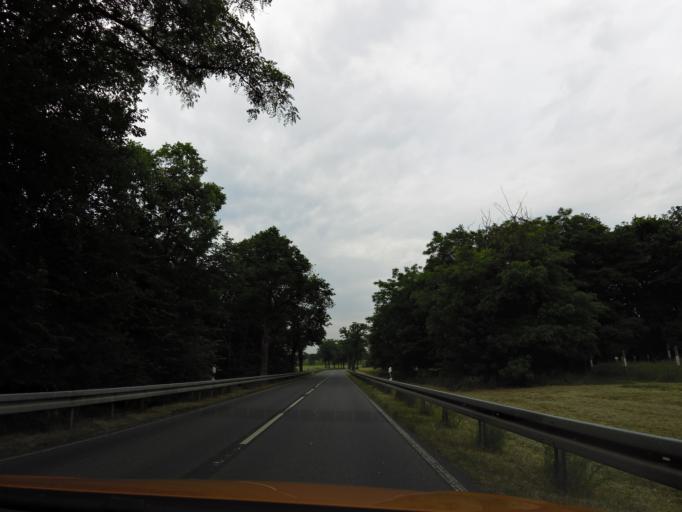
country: DE
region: Brandenburg
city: Rangsdorf
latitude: 52.2797
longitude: 13.3657
